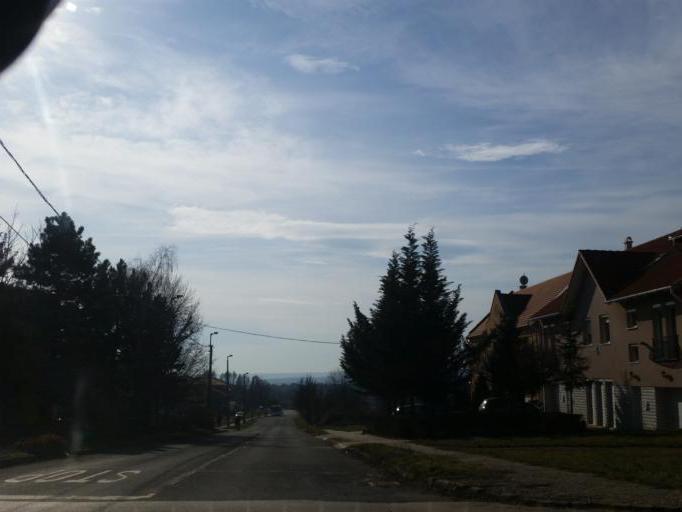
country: HU
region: Pest
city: Budakeszi
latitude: 47.5196
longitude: 18.9255
